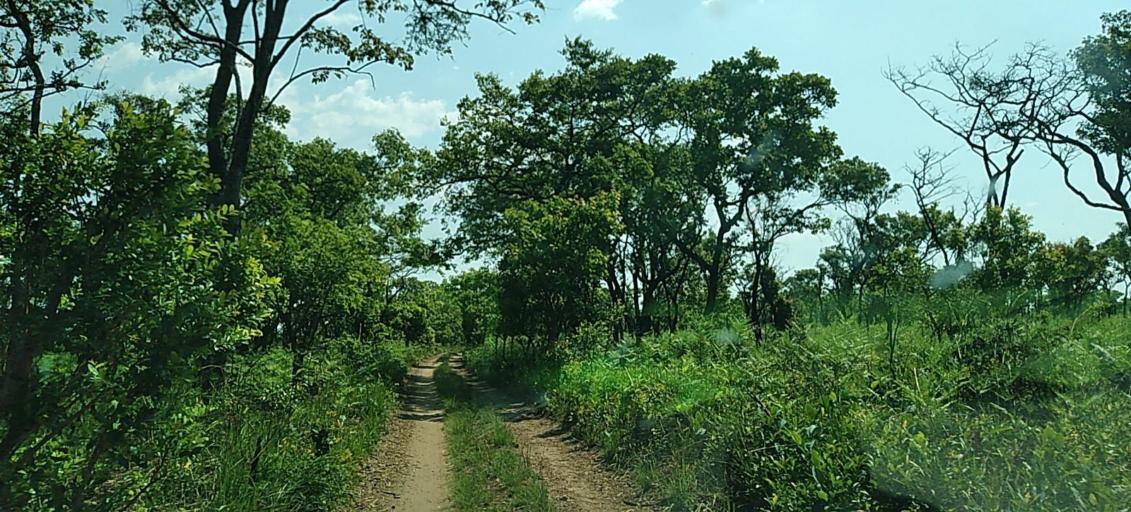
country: CD
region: Katanga
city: Kolwezi
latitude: -11.2631
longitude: 25.0039
